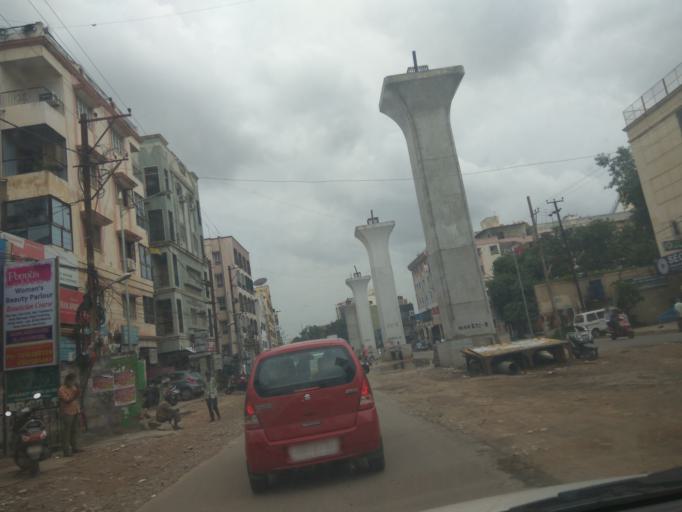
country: IN
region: Telangana
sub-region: Hyderabad
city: Malkajgiri
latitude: 17.4154
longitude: 78.4983
